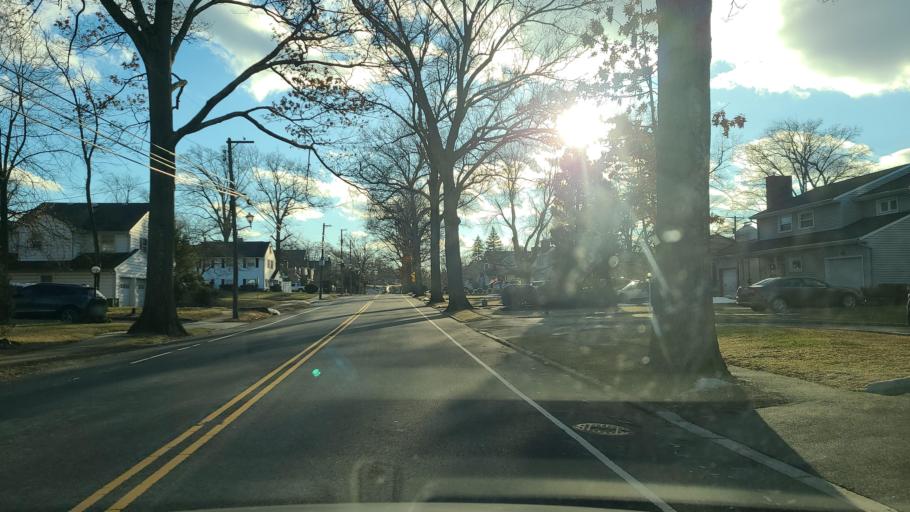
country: US
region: New Jersey
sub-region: Union County
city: Springfield
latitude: 40.6984
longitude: -74.3187
